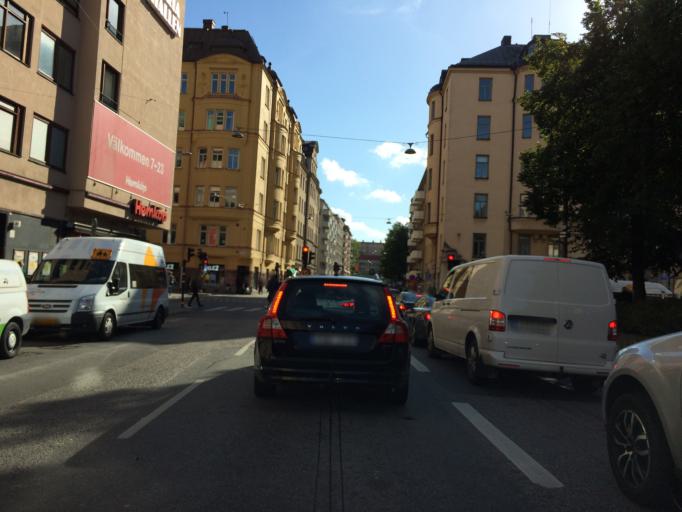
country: SE
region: Stockholm
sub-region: Stockholms Kommun
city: Stockholm
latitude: 59.3186
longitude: 18.0569
